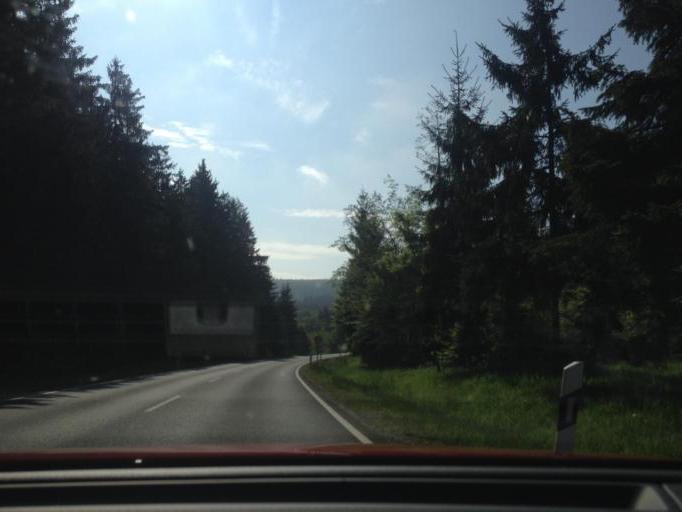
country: DE
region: Bavaria
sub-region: Upper Palatinate
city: Neusorg
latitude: 49.9075
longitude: 11.9633
